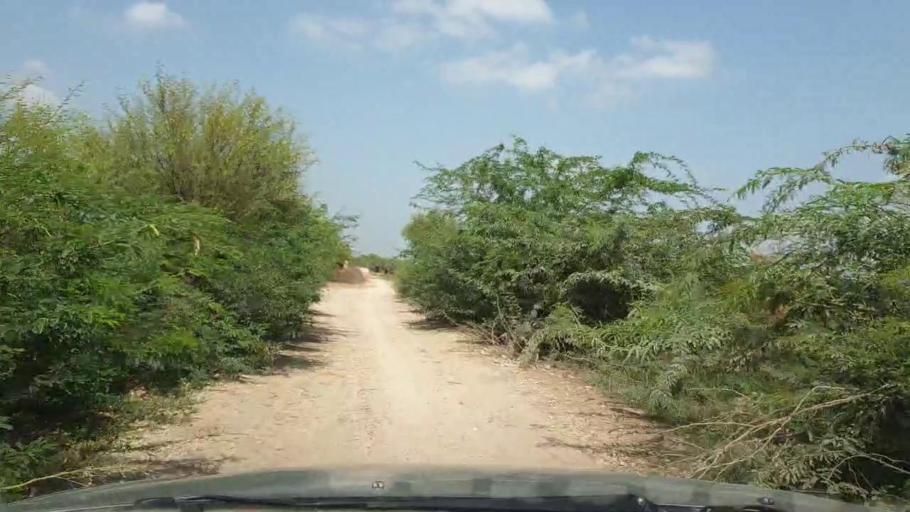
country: PK
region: Sindh
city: Rajo Khanani
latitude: 25.0222
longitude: 68.9165
